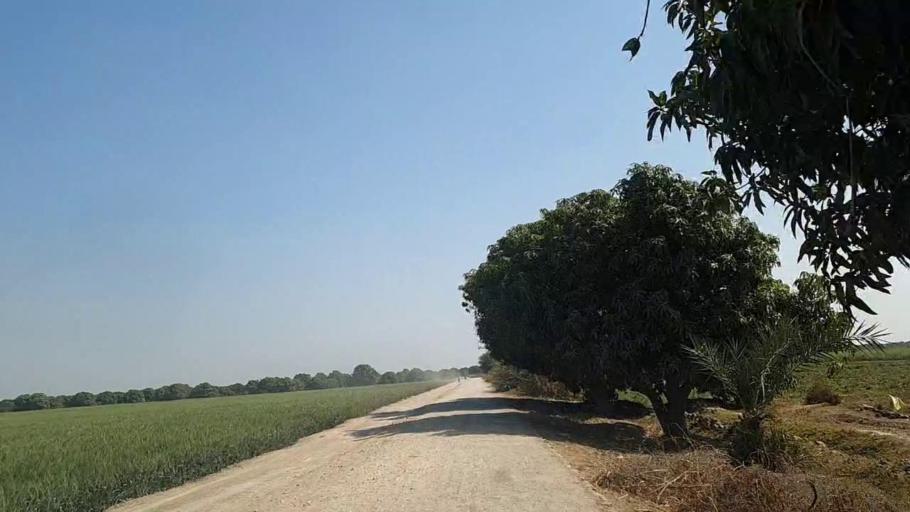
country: PK
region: Sindh
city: Digri
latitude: 25.1700
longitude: 69.2041
